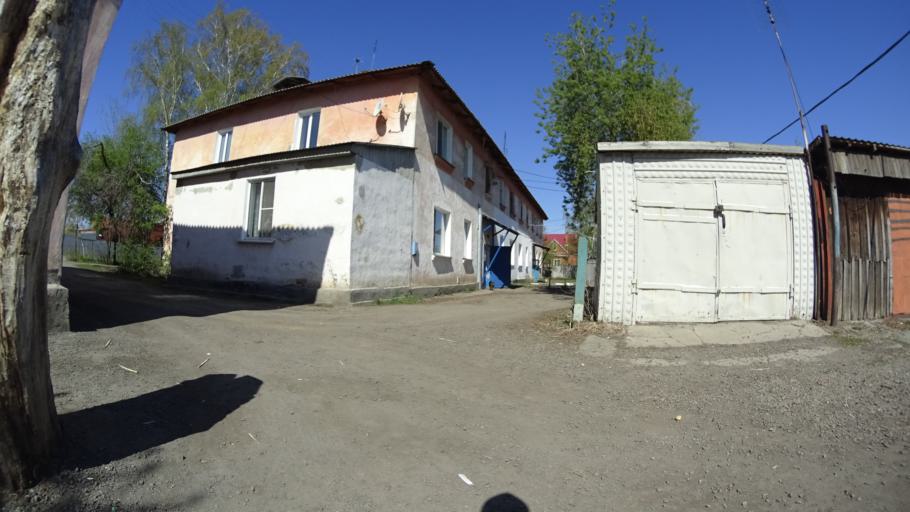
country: RU
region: Chelyabinsk
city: Troitsk
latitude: 54.1216
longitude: 61.5561
